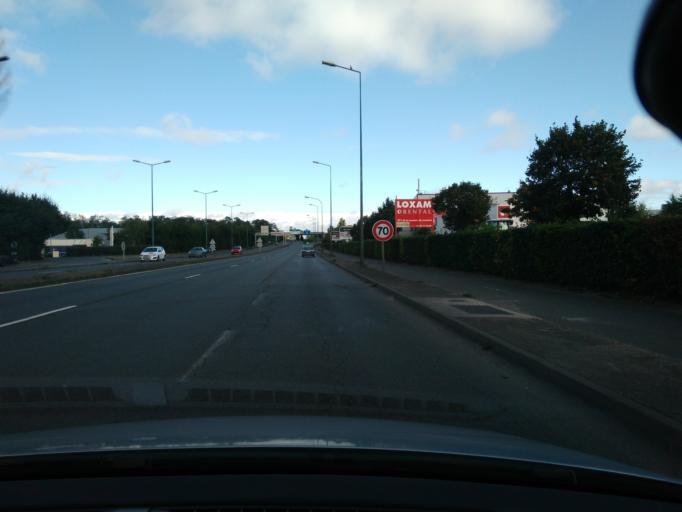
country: FR
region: Ile-de-France
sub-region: Departement de l'Essonne
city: Massy
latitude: 48.7199
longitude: 2.2991
